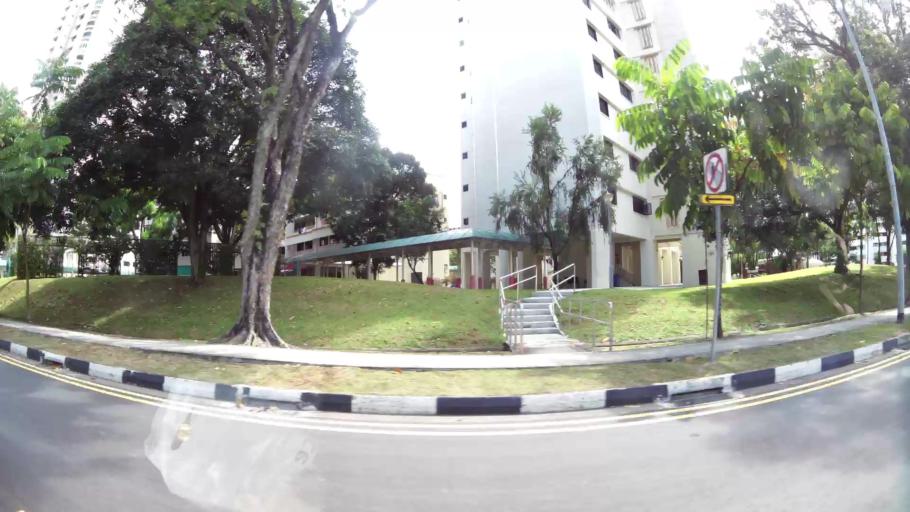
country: SG
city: Singapore
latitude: 1.3389
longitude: 103.7341
